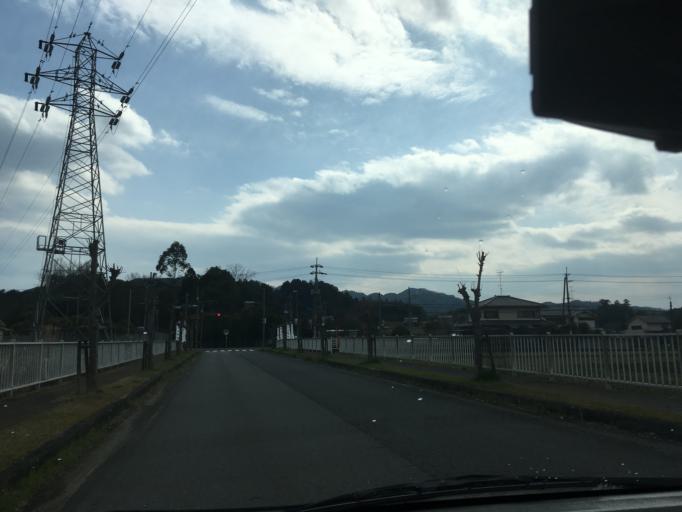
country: JP
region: Nara
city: Gose
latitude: 34.4493
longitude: 135.7914
